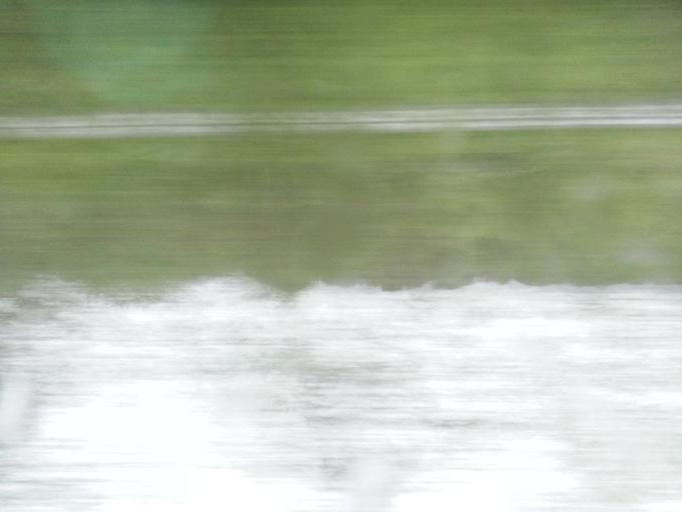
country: NO
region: Sor-Trondelag
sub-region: Oppdal
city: Oppdal
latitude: 62.6090
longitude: 9.7433
